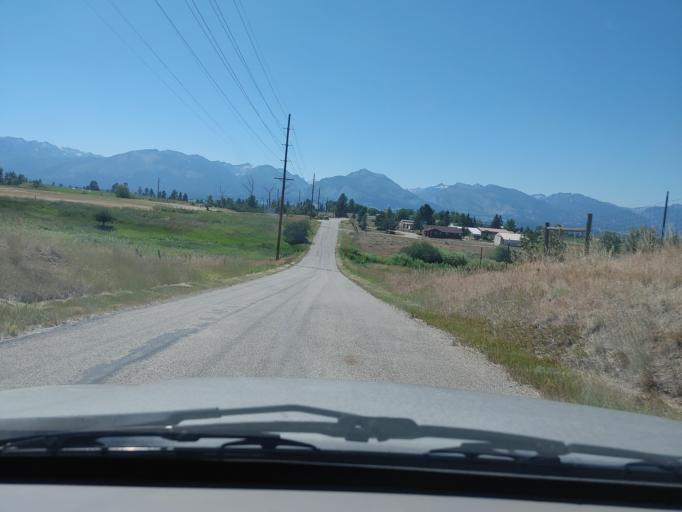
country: US
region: Montana
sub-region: Ravalli County
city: Hamilton
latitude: 46.2767
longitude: -114.0357
